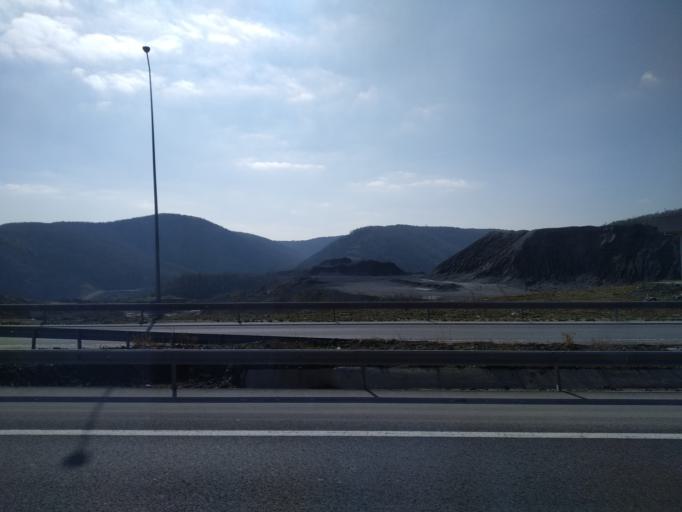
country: TR
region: Istanbul
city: Arikoey
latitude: 41.2237
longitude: 28.9886
